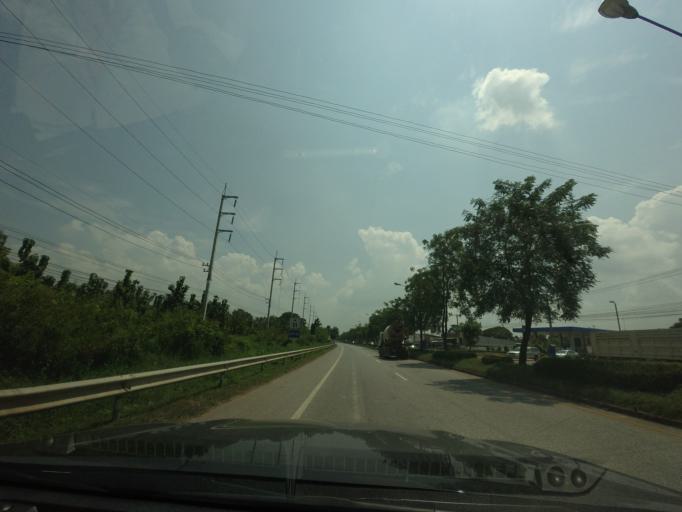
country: TH
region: Uttaradit
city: Uttaradit
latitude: 17.5973
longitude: 100.1273
